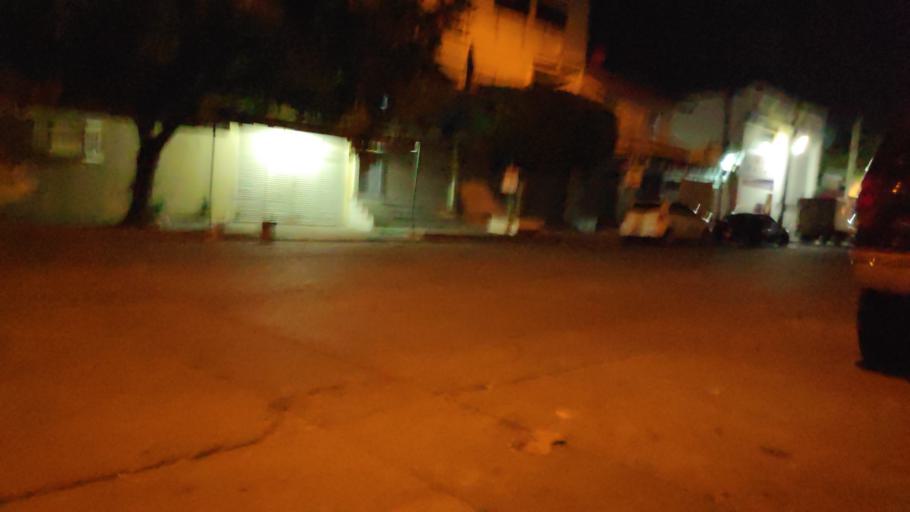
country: MX
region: Sinaloa
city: Culiacan
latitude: 24.7996
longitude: -107.3996
